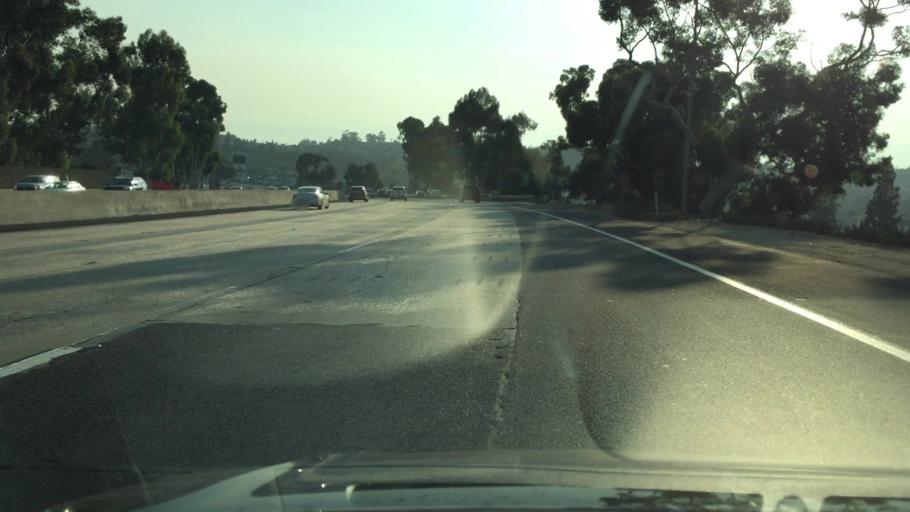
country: US
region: California
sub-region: San Diego County
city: El Cajon
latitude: 32.8032
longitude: -116.9695
